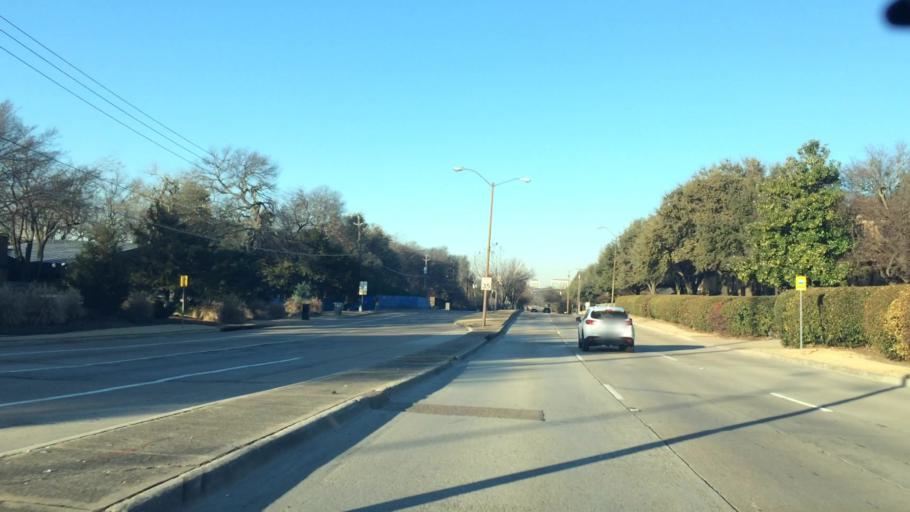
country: US
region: Texas
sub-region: Dallas County
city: Addison
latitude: 32.9399
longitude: -96.7865
